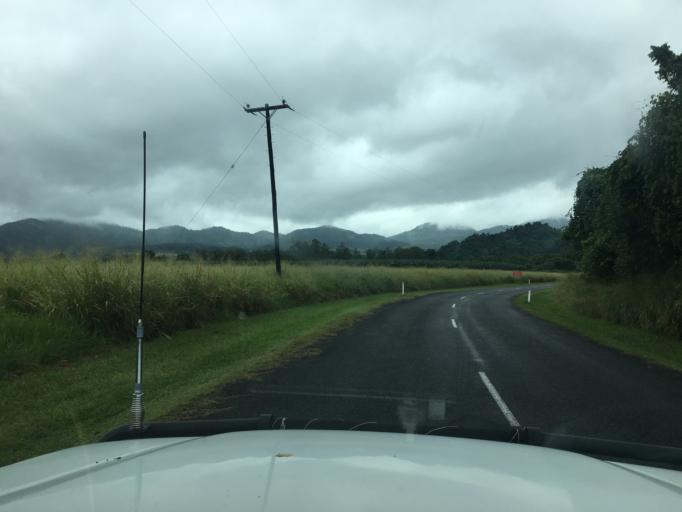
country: AU
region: Queensland
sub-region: Cassowary Coast
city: Innisfail
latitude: -17.4408
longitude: 145.8609
